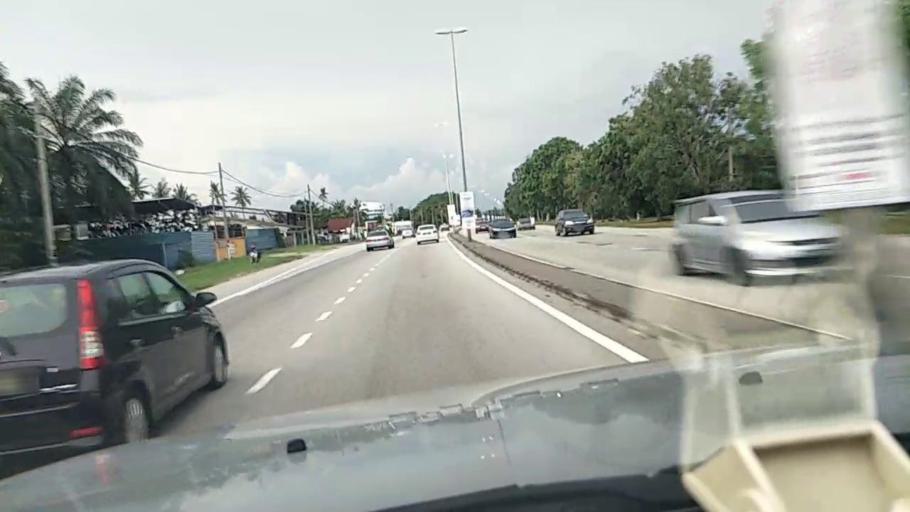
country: MY
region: Perak
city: Kampong Dungun
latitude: 3.1165
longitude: 101.3672
